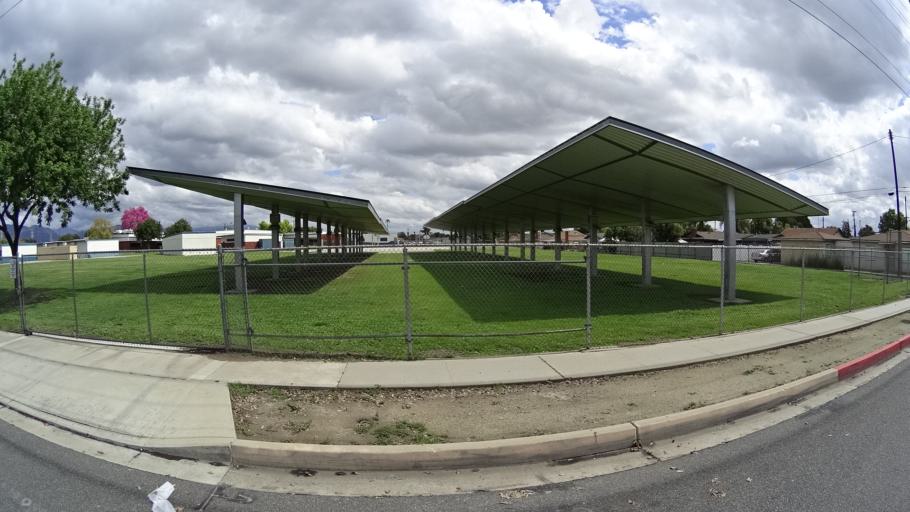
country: US
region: California
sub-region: Los Angeles County
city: Baldwin Park
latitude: 34.0974
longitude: -117.9780
